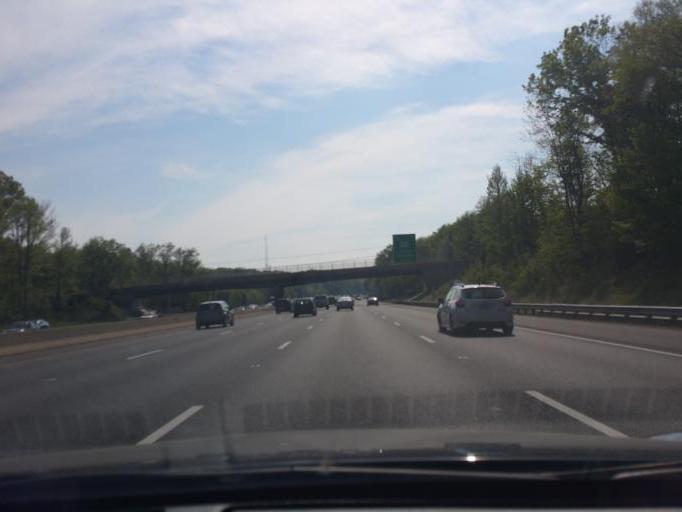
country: US
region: Maryland
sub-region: Harford County
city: Joppatowne
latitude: 39.4459
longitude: -76.3333
